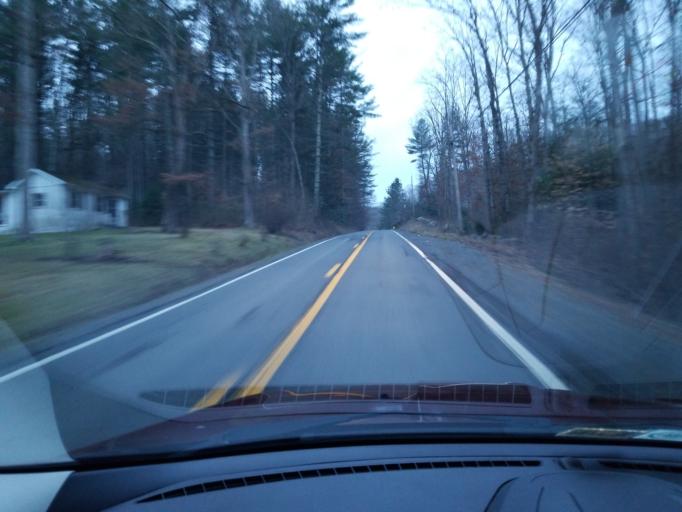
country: US
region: West Virginia
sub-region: Greenbrier County
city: Lewisburg
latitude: 37.7627
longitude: -80.3965
